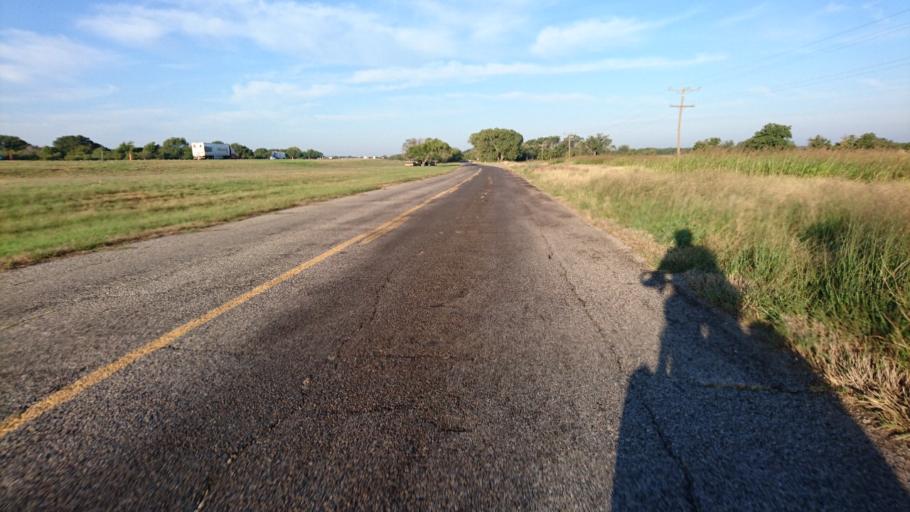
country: US
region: Oklahoma
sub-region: Beckham County
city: Sayre
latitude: 35.2625
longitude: -99.7059
